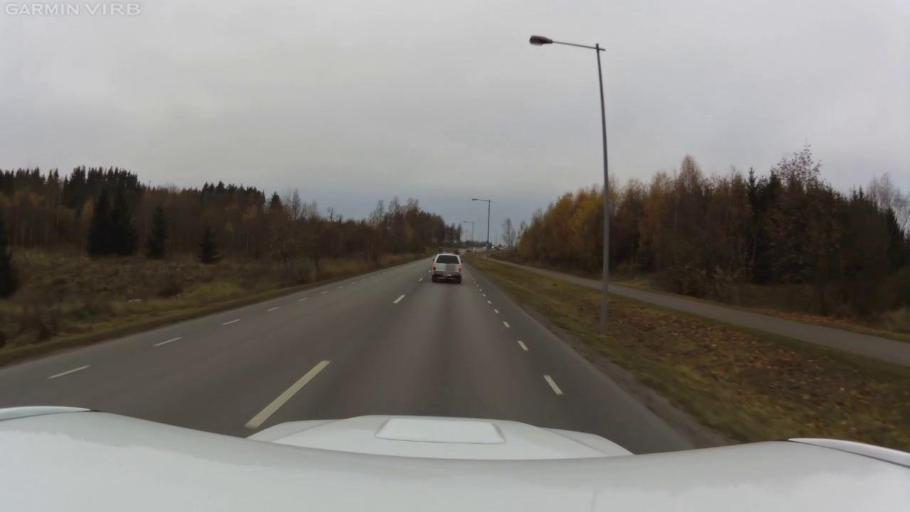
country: SE
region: OEstergoetland
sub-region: Linkopings Kommun
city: Linkoping
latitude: 58.3903
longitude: 15.5953
